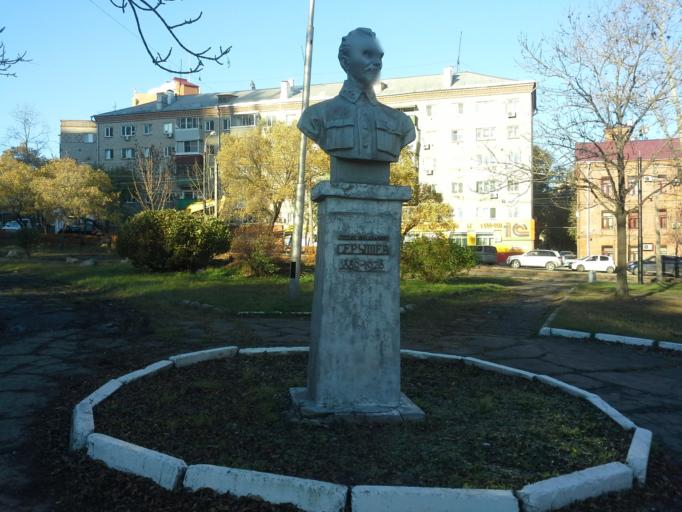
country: RU
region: Khabarovsk Krai
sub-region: Khabarovskiy Rayon
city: Khabarovsk
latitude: 48.4876
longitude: 135.0621
